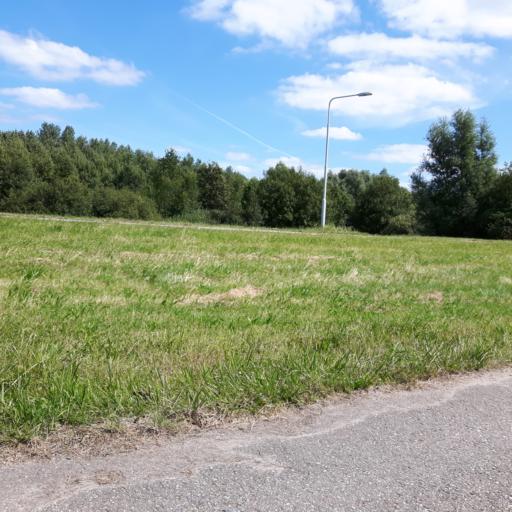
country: NL
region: North Brabant
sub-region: Gemeente Woensdrecht
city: Woensdrecht
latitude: 51.4348
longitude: 4.2379
